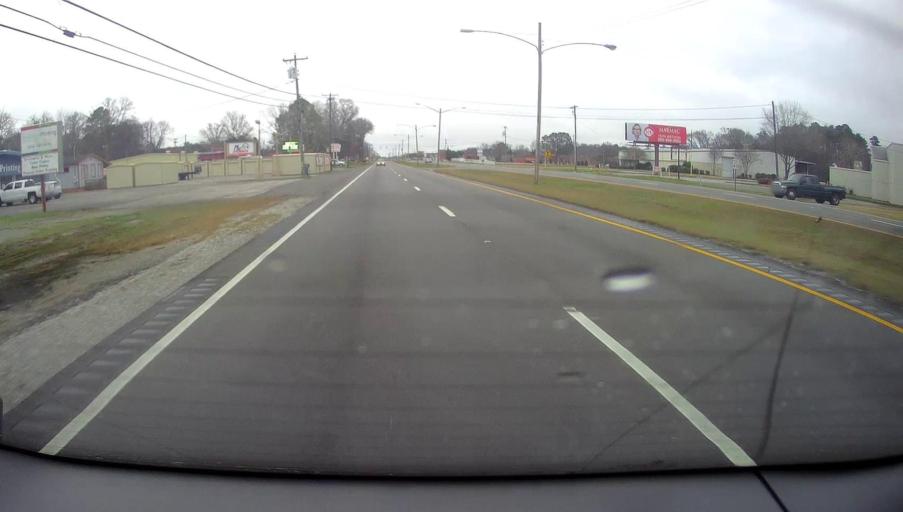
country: US
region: Alabama
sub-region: Morgan County
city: Flint City
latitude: 34.5496
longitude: -86.9738
